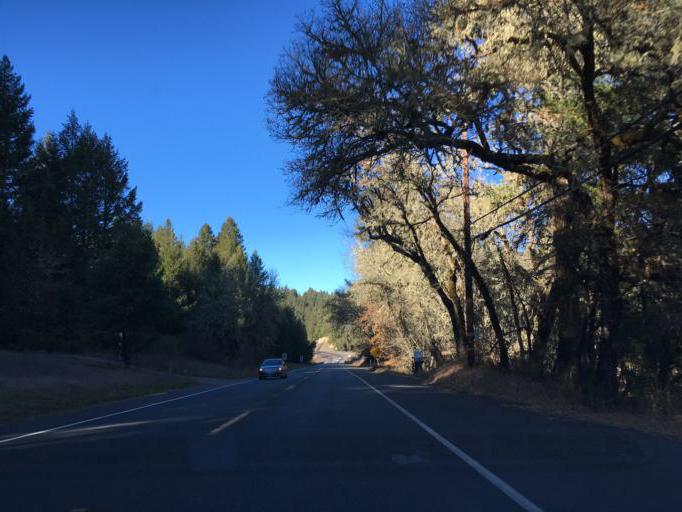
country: US
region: California
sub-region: Mendocino County
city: Brooktrails
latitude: 39.4603
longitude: -123.3496
